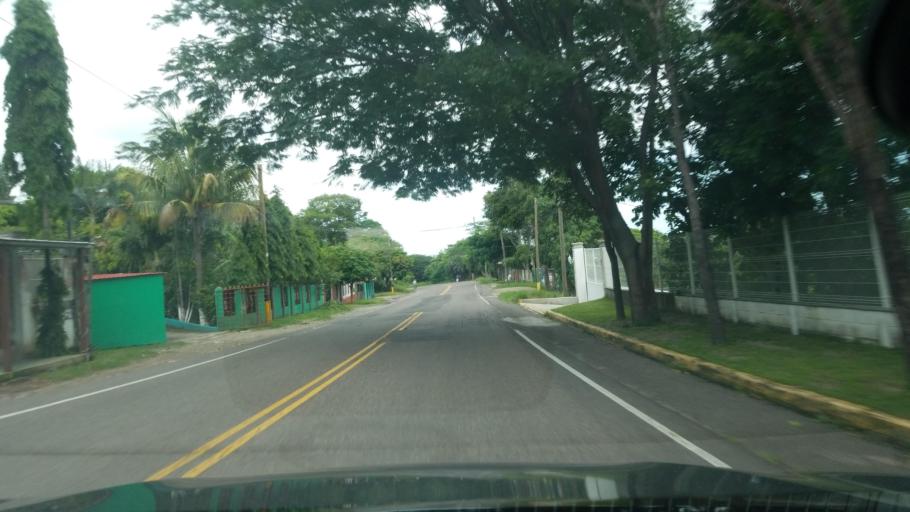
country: HN
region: Choluteca
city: Corpus
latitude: 13.3659
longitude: -86.9759
